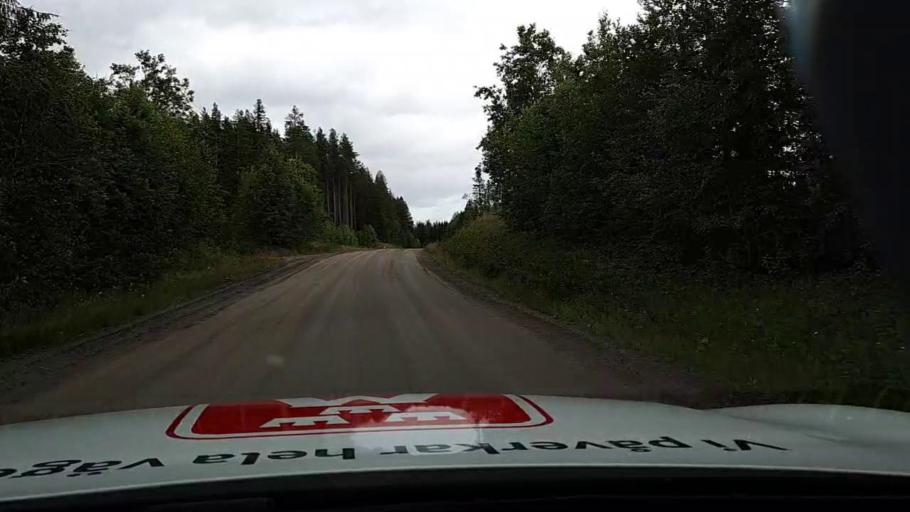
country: SE
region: Vaesternorrland
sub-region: Solleftea Kommun
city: As
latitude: 63.5103
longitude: 16.4055
